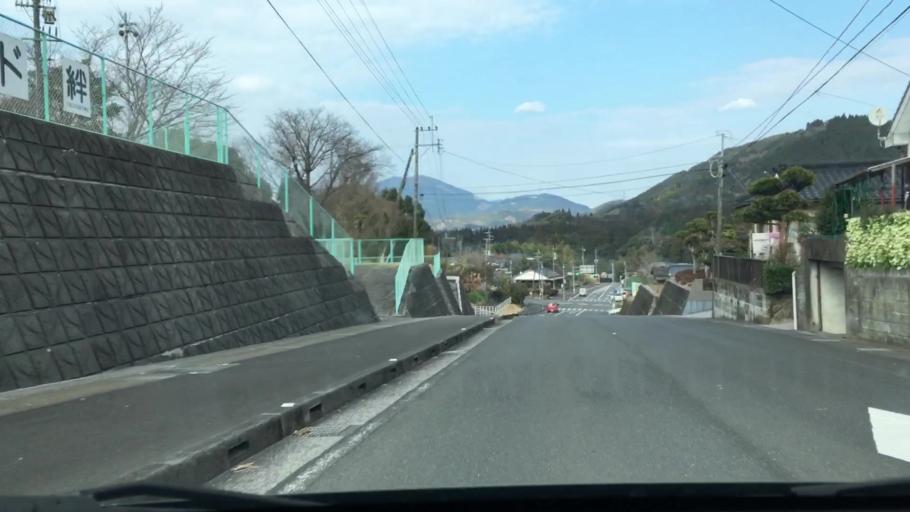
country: JP
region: Miyazaki
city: Kushima
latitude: 31.5249
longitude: 131.2369
